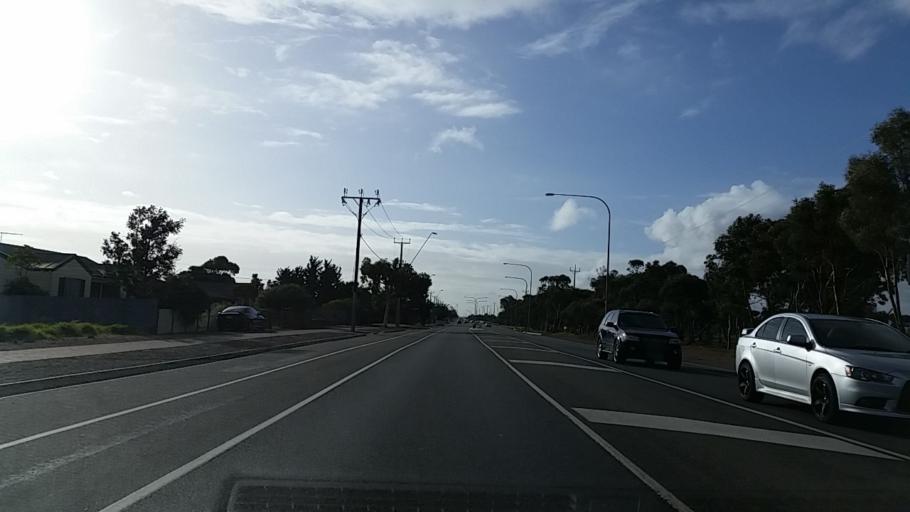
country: AU
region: South Australia
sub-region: Onkaparinga
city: Seaford
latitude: -35.1851
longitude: 138.4770
